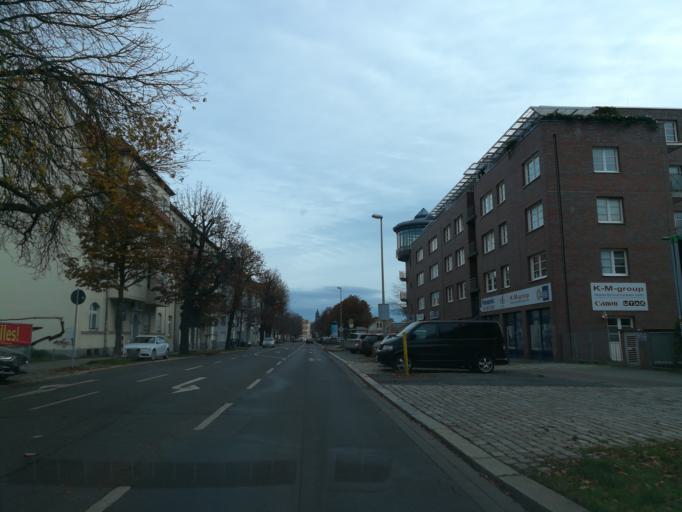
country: DE
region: Saxony-Anhalt
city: Magdeburg
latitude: 52.1234
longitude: 11.6070
